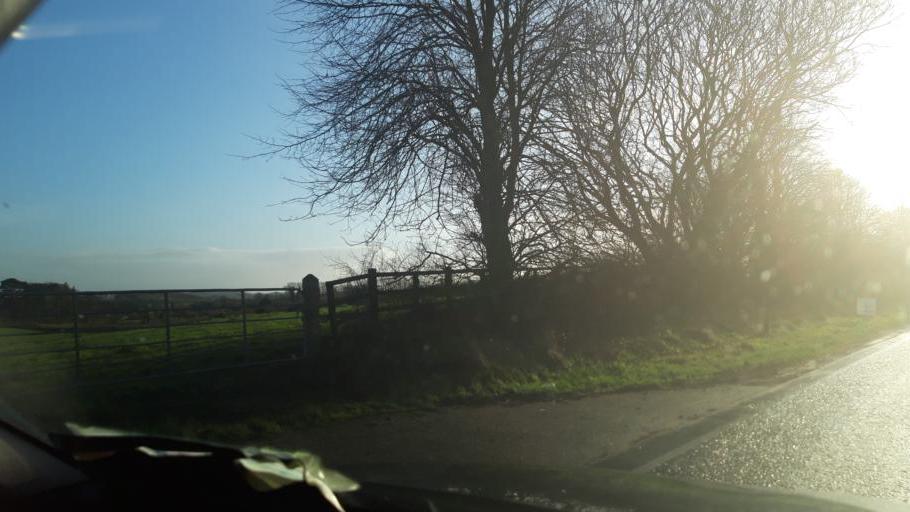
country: GB
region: Northern Ireland
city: Maghera
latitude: 54.8562
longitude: -6.6664
